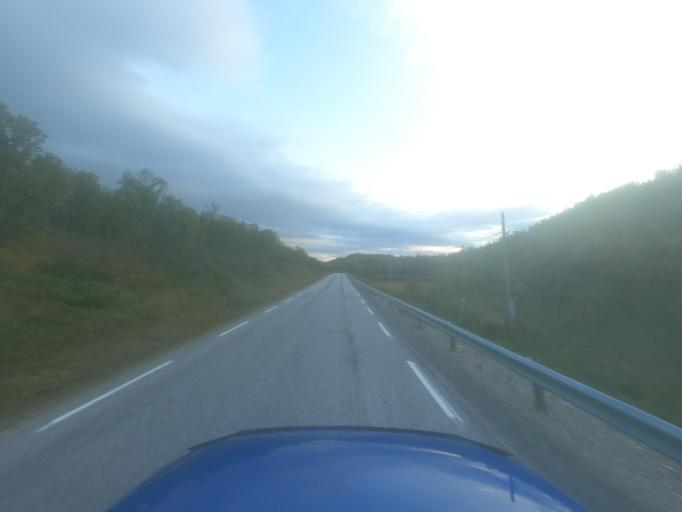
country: NO
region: Finnmark Fylke
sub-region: Porsanger
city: Lakselv
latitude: 70.2811
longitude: 25.0655
